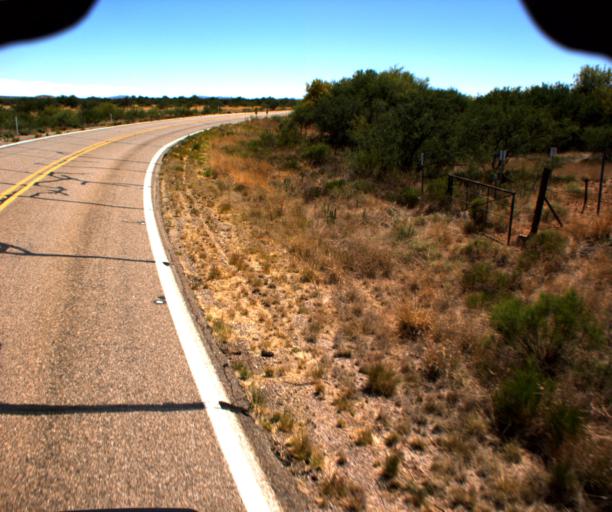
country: US
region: Arizona
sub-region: Pima County
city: Arivaca Junction
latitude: 31.6666
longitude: -111.4878
